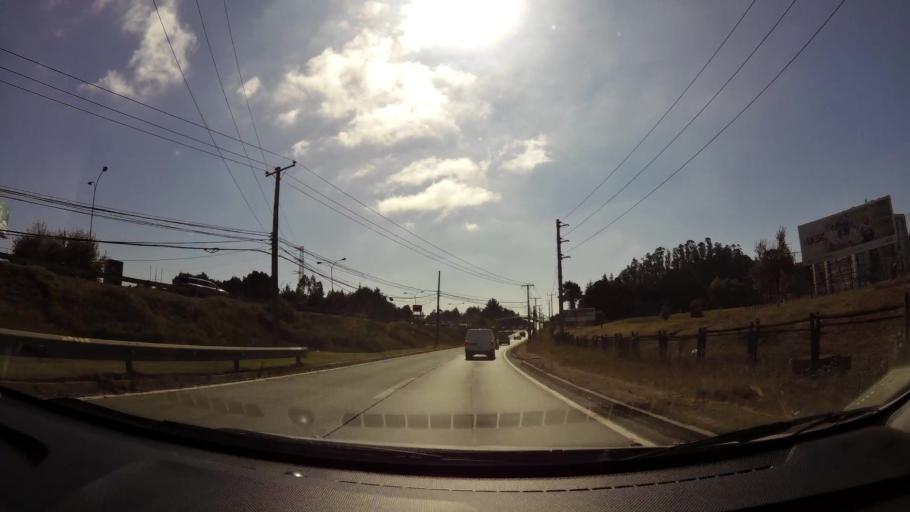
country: CL
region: Biobio
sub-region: Provincia de Concepcion
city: Concepcion
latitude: -36.7993
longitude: -73.0577
